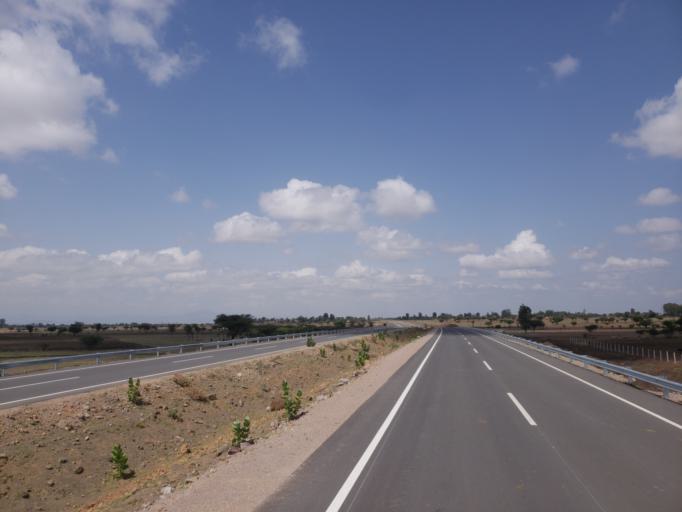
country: ET
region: Oromiya
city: Mojo
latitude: 8.5503
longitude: 39.1066
